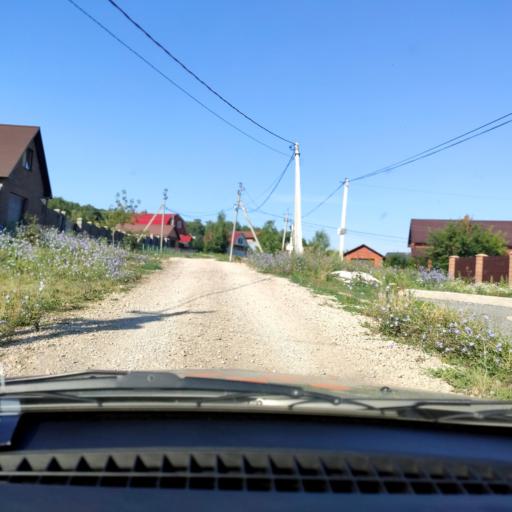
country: RU
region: Bashkortostan
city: Avdon
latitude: 54.5932
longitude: 55.7026
